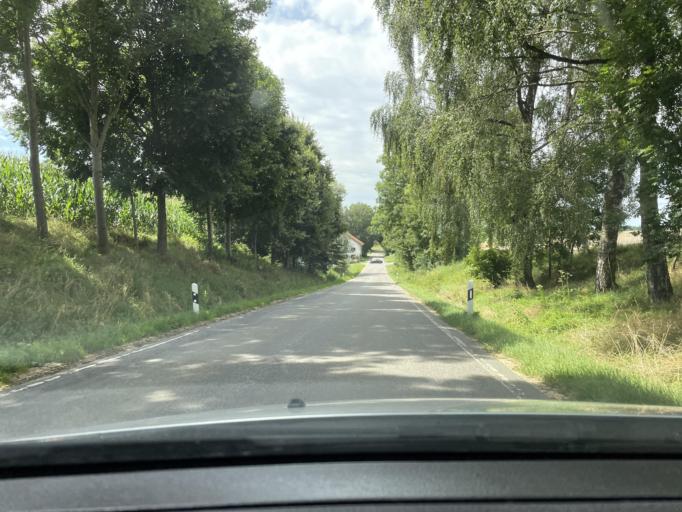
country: DE
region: Bavaria
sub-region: Lower Bavaria
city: Geisenhausen
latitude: 48.4366
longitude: 12.2872
